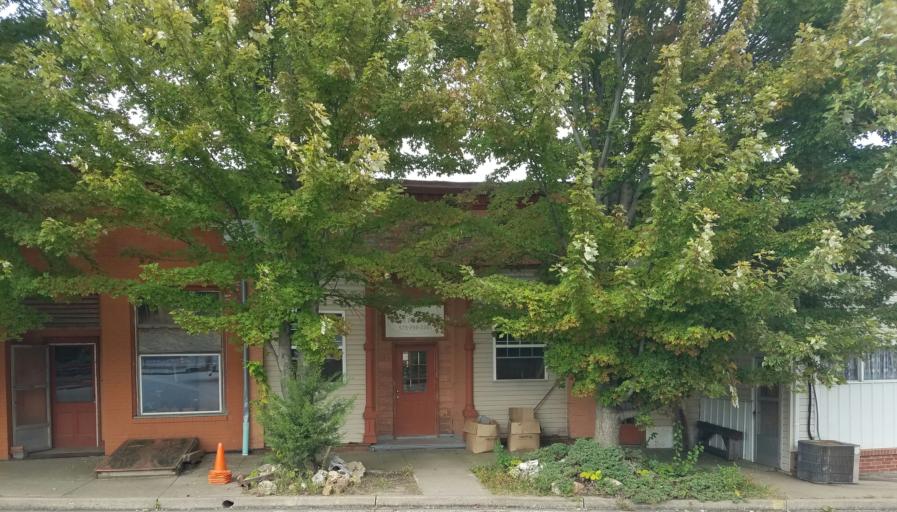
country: US
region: Missouri
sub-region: Moniteau County
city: California
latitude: 38.6293
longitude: -92.5664
